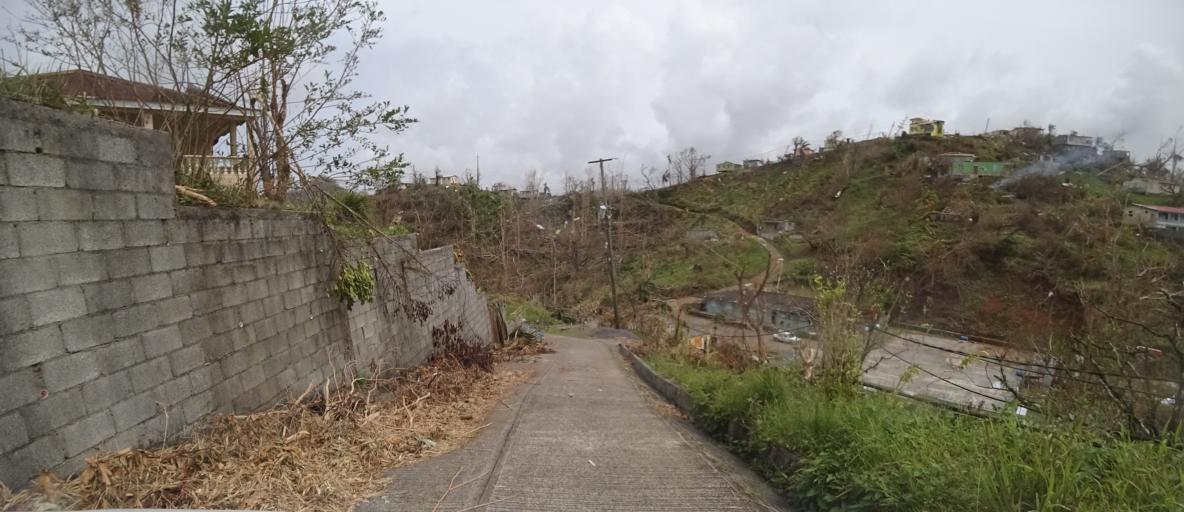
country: DM
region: Saint Andrew
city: Calibishie
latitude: 15.5896
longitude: -61.4056
